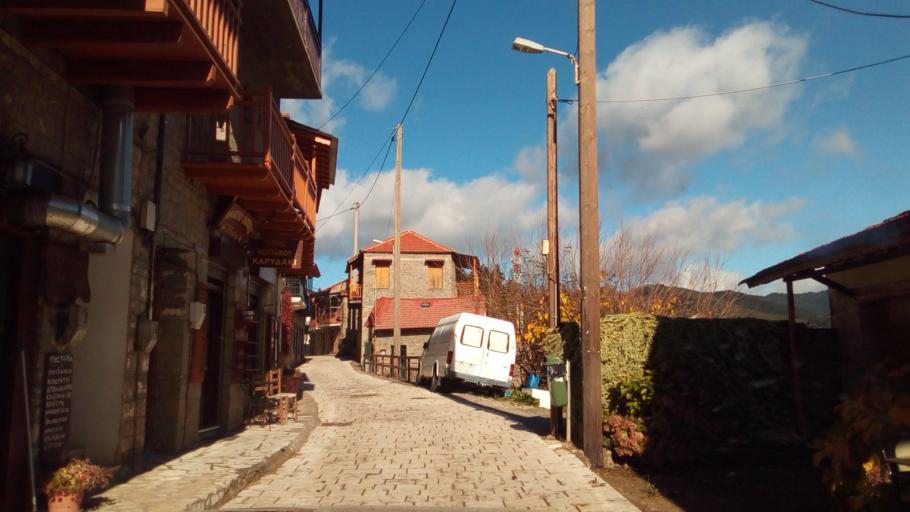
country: GR
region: West Greece
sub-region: Nomos Aitolias kai Akarnanias
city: Nafpaktos
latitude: 38.5917
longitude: 21.9241
